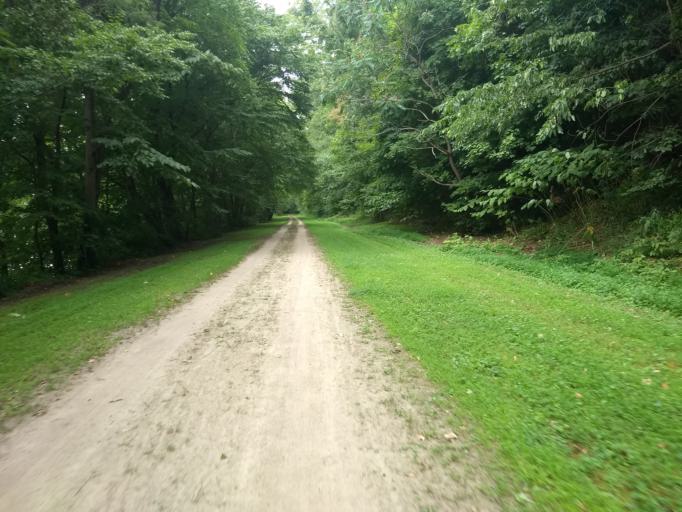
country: US
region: Pennsylvania
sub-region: Armstrong County
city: Freeport
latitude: 40.6425
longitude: -79.6867
